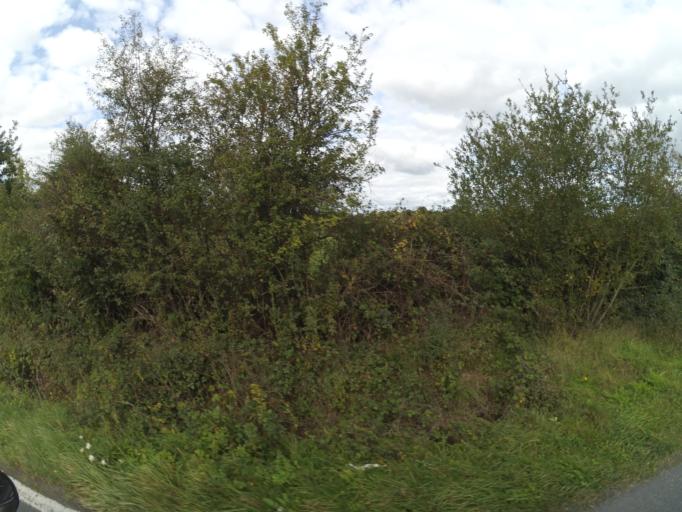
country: FR
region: Pays de la Loire
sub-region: Departement de la Loire-Atlantique
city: Fay-de-Bretagne
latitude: 47.4144
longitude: -1.7835
